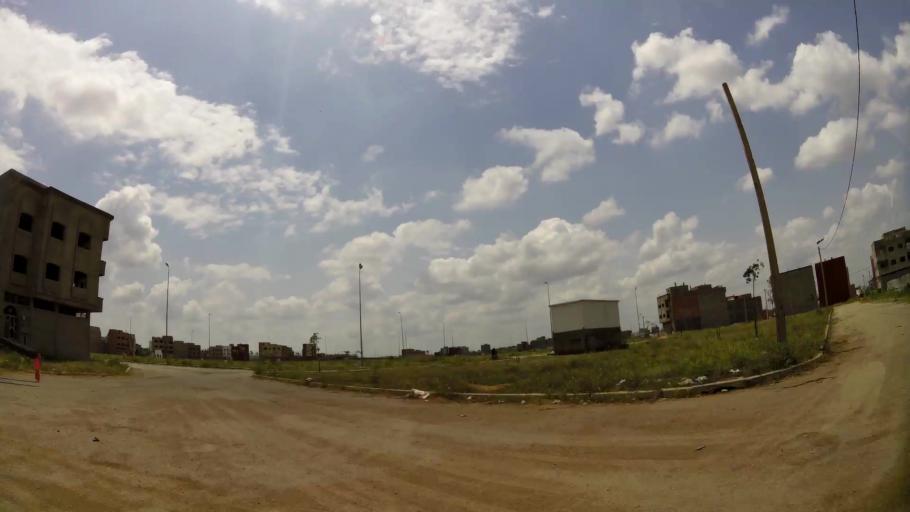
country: MA
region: Rabat-Sale-Zemmour-Zaer
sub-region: Khemisset
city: Tiflet
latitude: 34.0055
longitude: -6.5364
